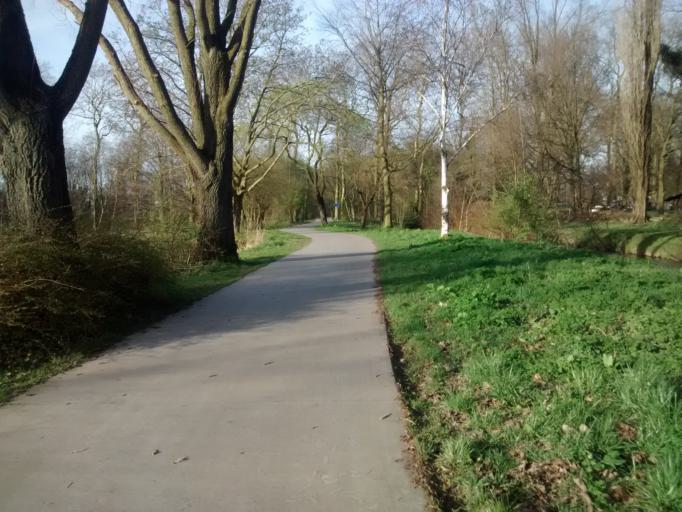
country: NL
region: Utrecht
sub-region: Gemeente Nieuwegein
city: Nieuwegein
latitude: 52.0213
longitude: 5.0846
